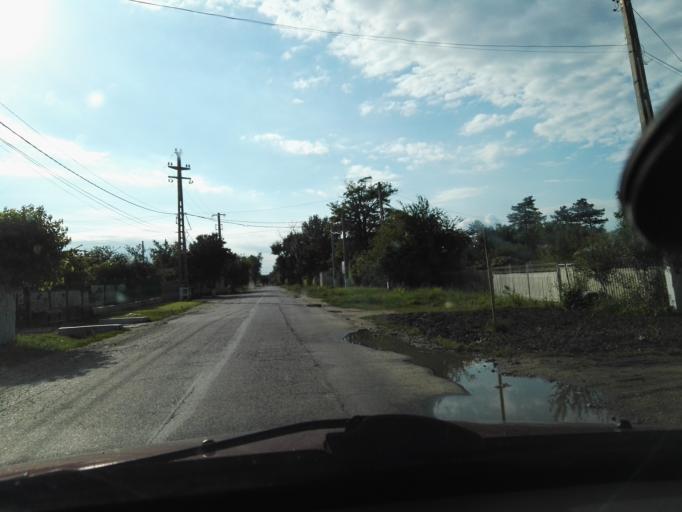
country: RO
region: Ilfov
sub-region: Comuna Copaceni
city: Copaceni
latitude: 44.2420
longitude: 26.1036
